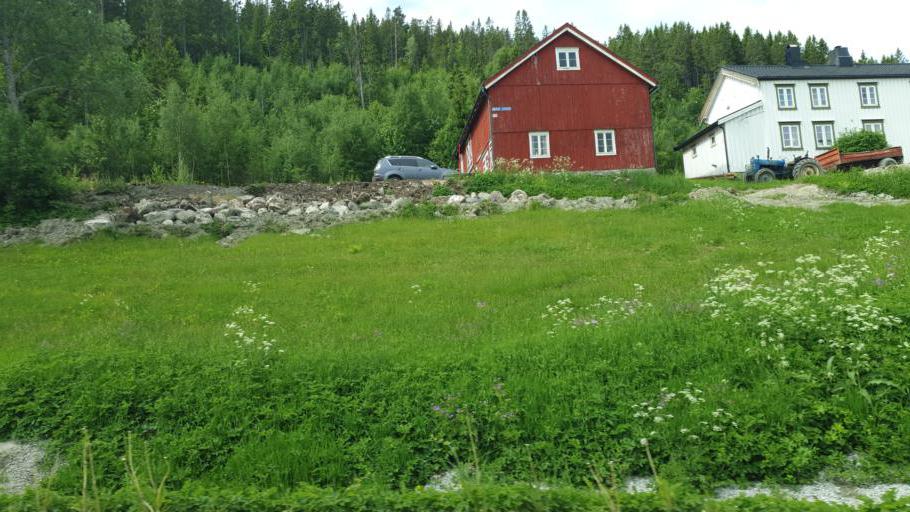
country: NO
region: Sor-Trondelag
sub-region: Trondheim
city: Trondheim
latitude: 63.5800
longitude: 10.4165
